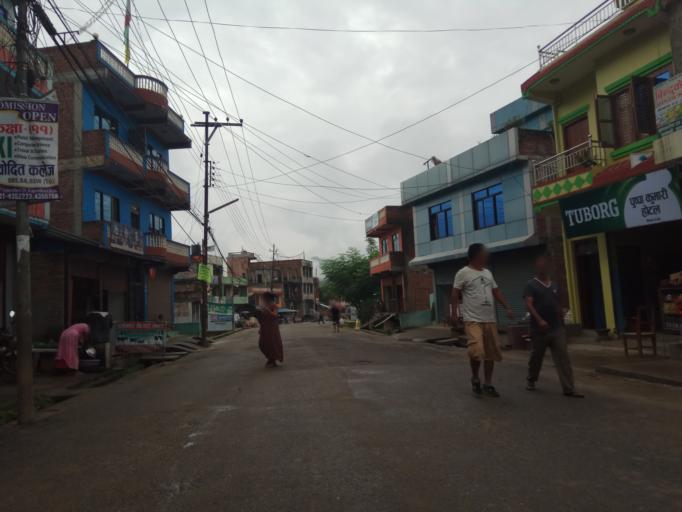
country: NP
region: Central Region
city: Kirtipur
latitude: 27.9090
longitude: 84.9003
